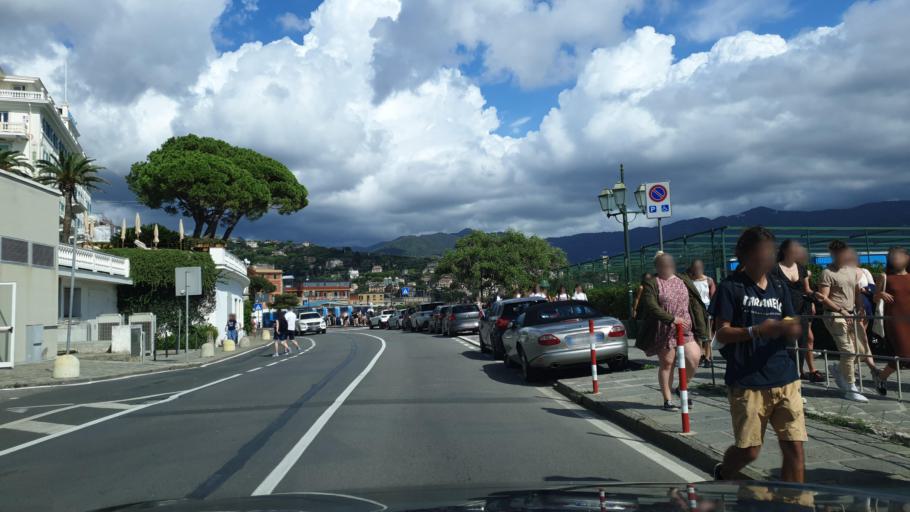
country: IT
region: Liguria
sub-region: Provincia di Genova
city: Santa Margherita Ligure
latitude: 44.3270
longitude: 9.2154
